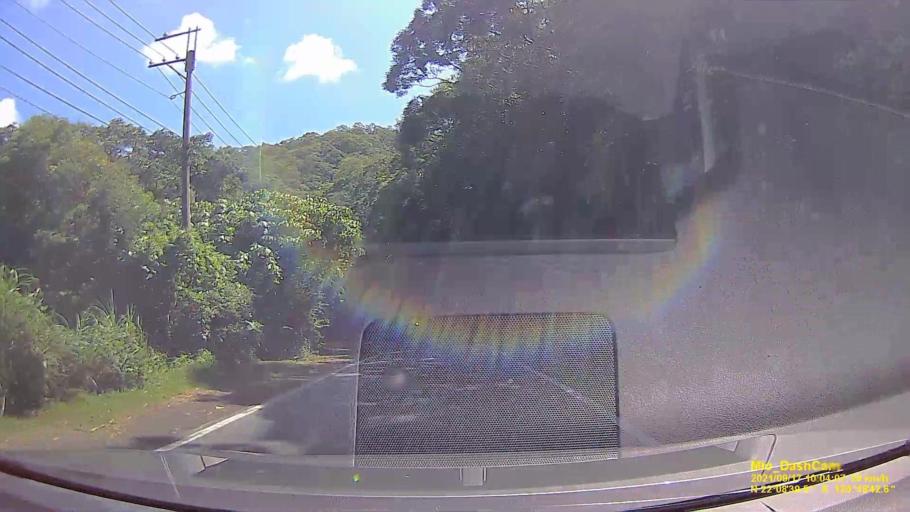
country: TW
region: Taiwan
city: Hengchun
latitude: 22.1443
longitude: 120.8119
